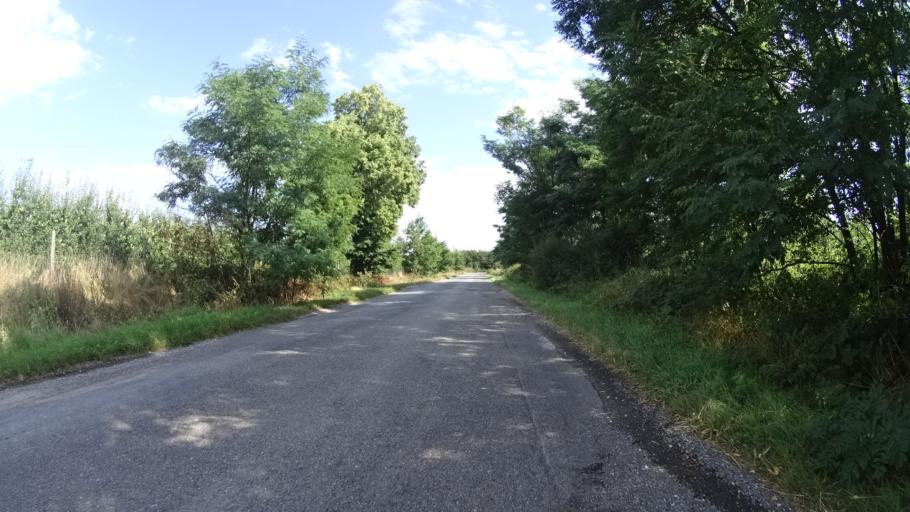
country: PL
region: Masovian Voivodeship
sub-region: Powiat grojecki
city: Mogielnica
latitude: 51.6823
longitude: 20.7614
